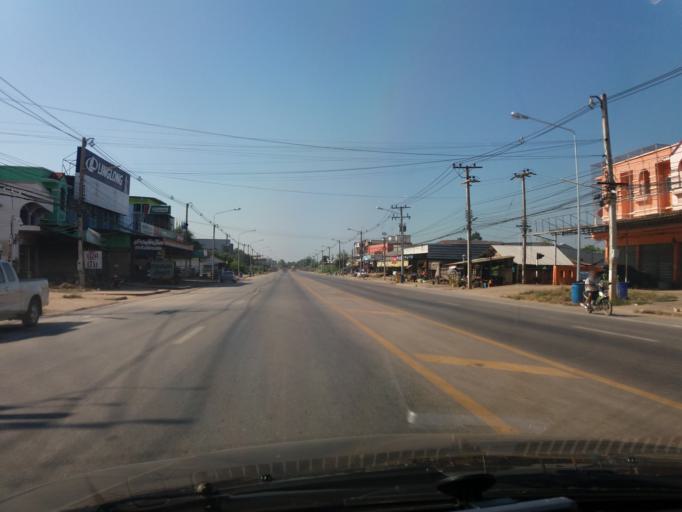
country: TH
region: Kamphaeng Phet
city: Khlong Khlung
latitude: 16.2267
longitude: 99.7311
